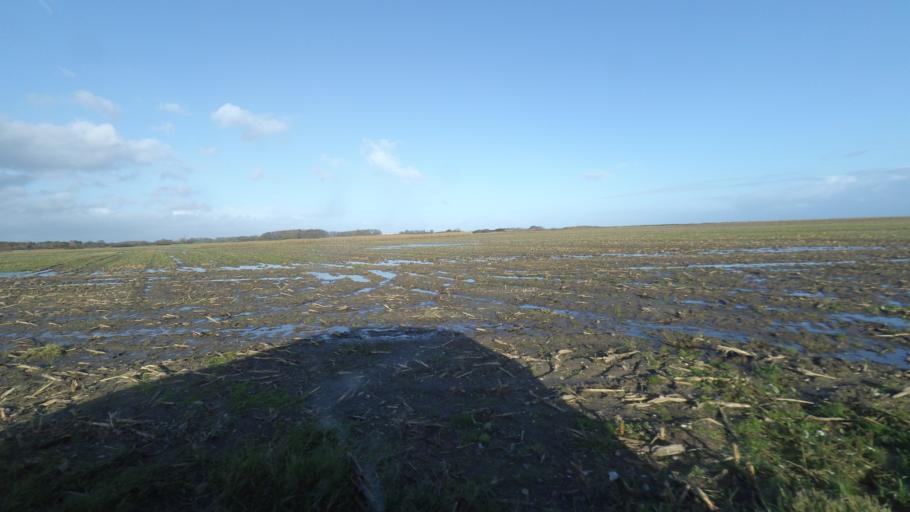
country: DK
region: Central Jutland
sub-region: Odder Kommune
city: Odder
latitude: 55.8476
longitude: 10.1878
